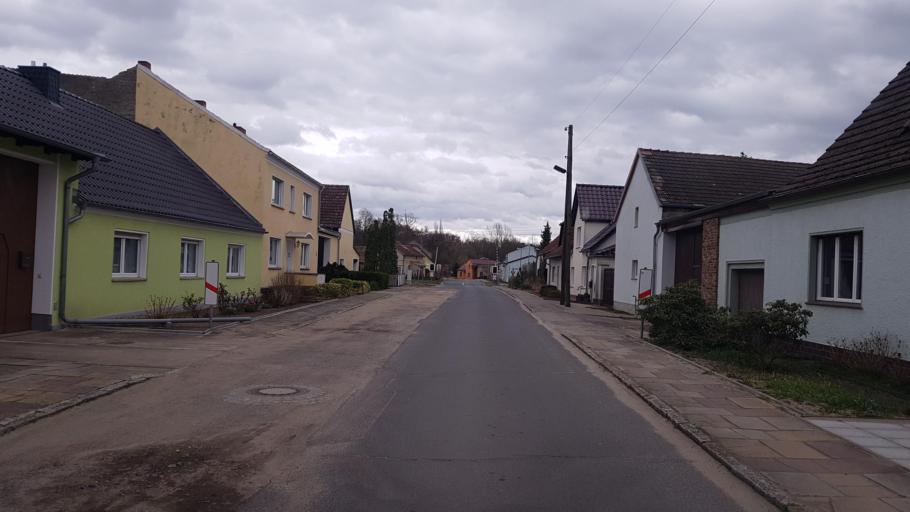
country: DE
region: Brandenburg
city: Bruck
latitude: 52.1723
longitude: 12.7329
